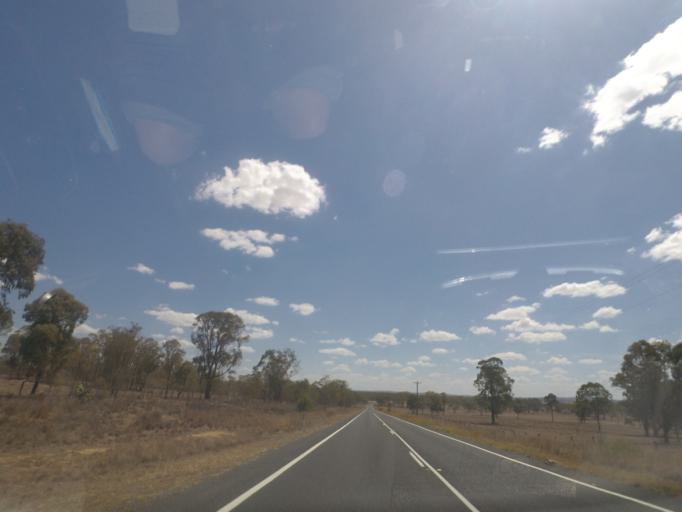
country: AU
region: Queensland
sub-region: Southern Downs
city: Warwick
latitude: -28.1796
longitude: 151.8237
